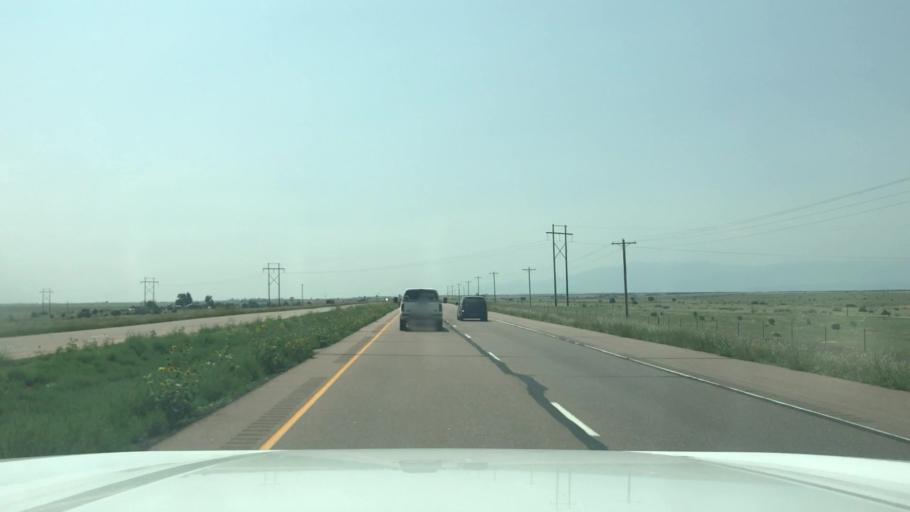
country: US
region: Colorado
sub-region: Pueblo County
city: Pueblo
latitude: 38.1026
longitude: -104.6840
